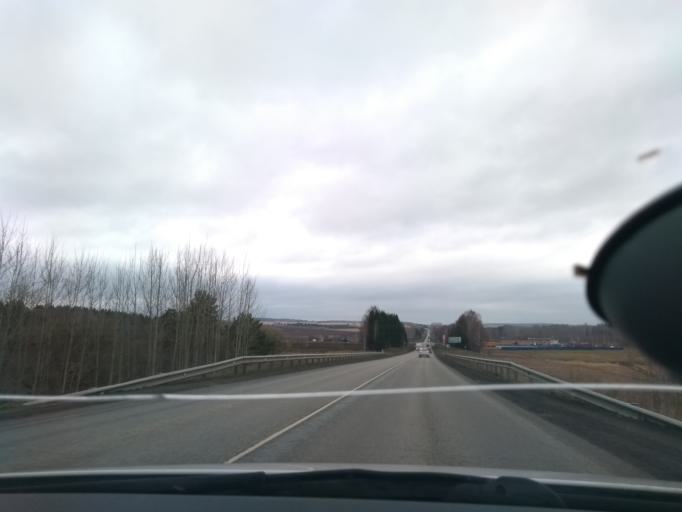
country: RU
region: Perm
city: Kungur
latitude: 57.4551
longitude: 56.7690
